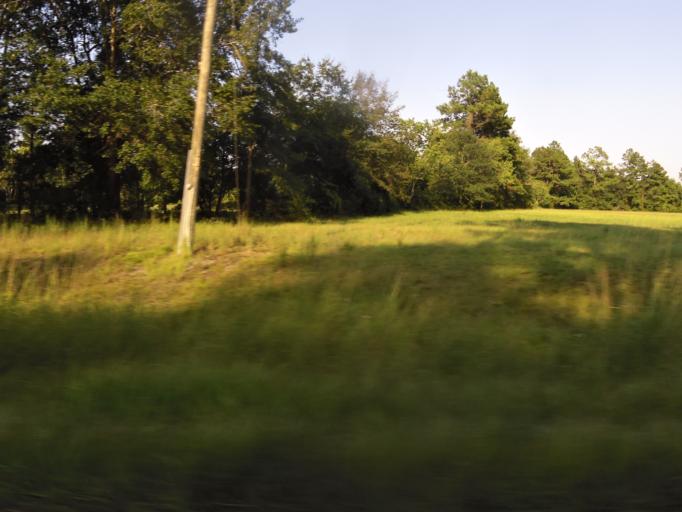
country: US
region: Florida
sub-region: Duval County
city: Baldwin
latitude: 30.3623
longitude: -82.0102
